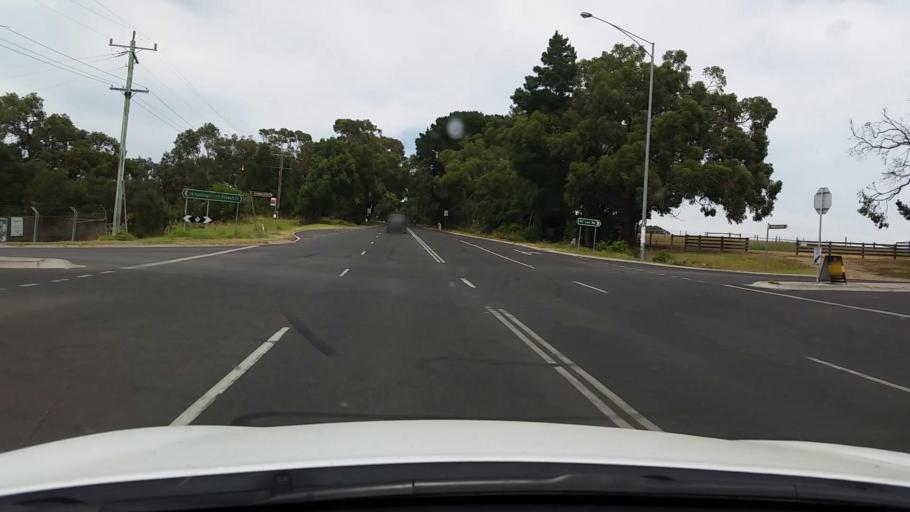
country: AU
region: Victoria
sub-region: Mornington Peninsula
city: Merricks
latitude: -38.4066
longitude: 145.0656
